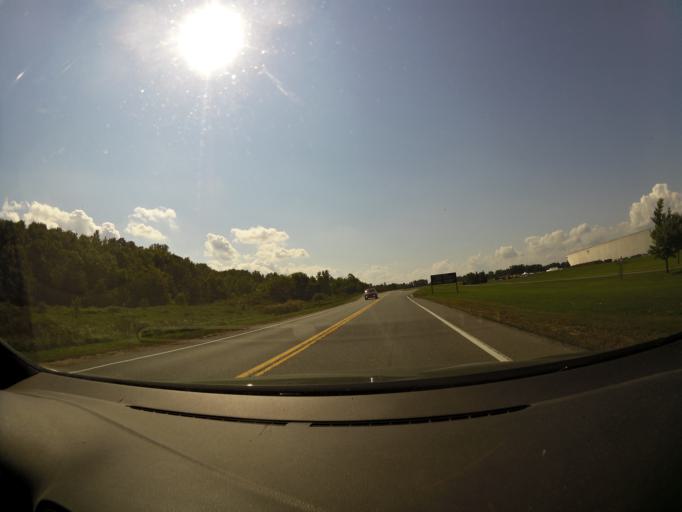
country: CA
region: Quebec
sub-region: Outaouais
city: Gatineau
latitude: 45.4576
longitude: -75.6391
